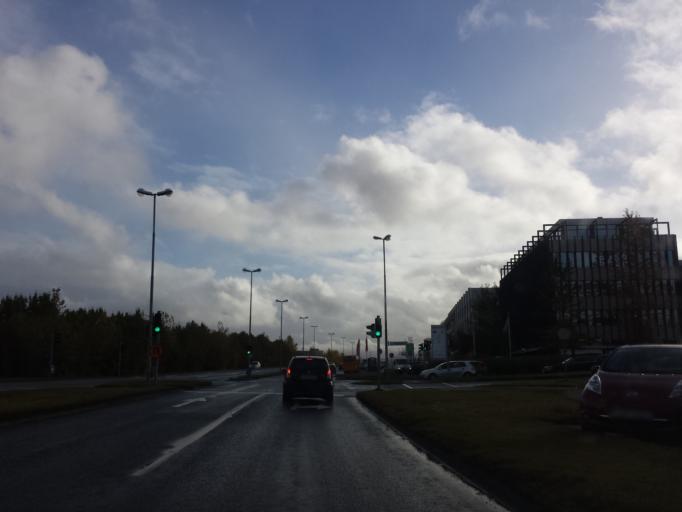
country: IS
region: Capital Region
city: Reykjavik
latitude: 64.1389
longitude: -21.8795
